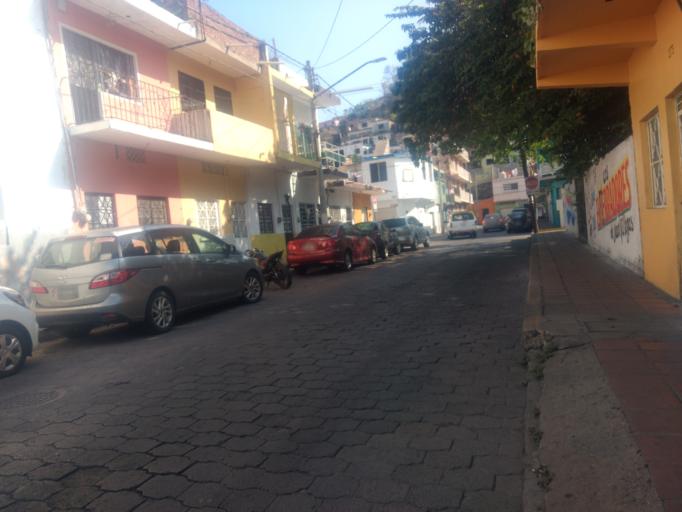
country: MX
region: Colima
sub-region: Manzanillo
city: Manzanillo
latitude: 19.0504
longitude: -104.3157
